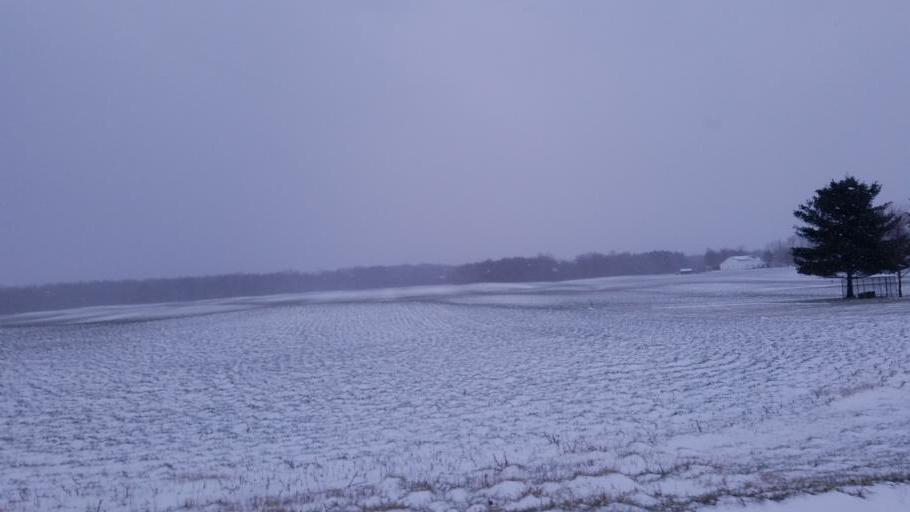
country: US
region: Ohio
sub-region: Knox County
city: Fredericktown
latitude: 40.4977
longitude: -82.6604
